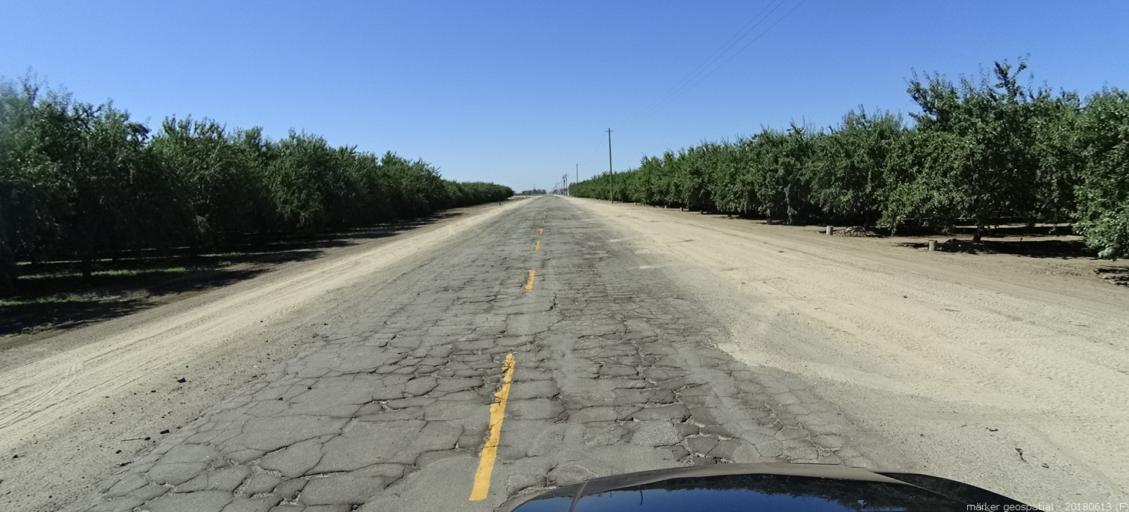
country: US
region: California
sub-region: Madera County
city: Chowchilla
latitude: 37.0791
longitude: -120.4009
